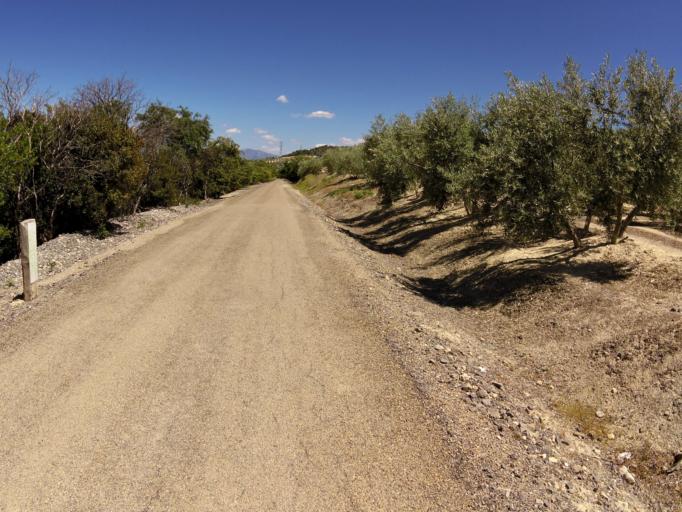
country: ES
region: Andalusia
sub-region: Provincia de Jaen
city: Torre del Campo
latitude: 37.7921
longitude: -3.8723
